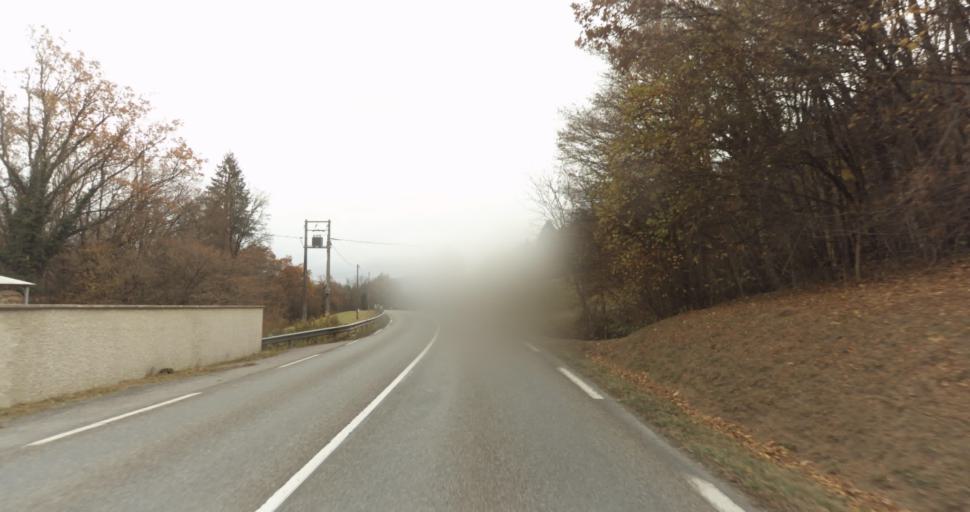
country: FR
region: Rhone-Alpes
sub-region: Departement de la Haute-Savoie
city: Groisy
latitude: 45.9951
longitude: 6.1743
